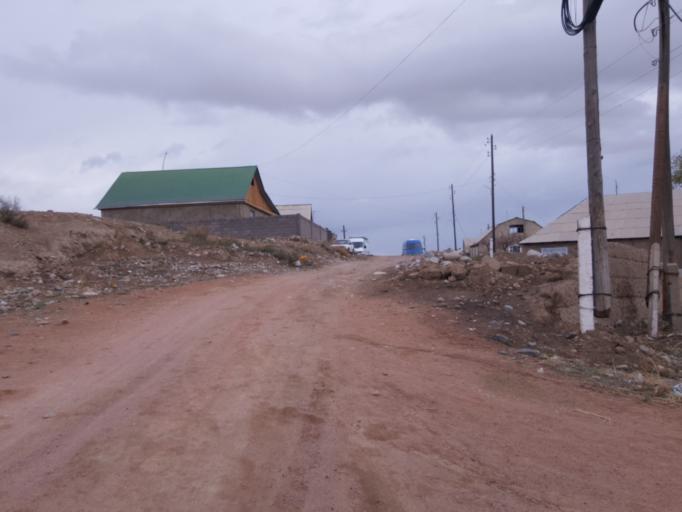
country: KG
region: Ysyk-Koel
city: Bokombayevskoye
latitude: 42.1111
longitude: 76.9812
